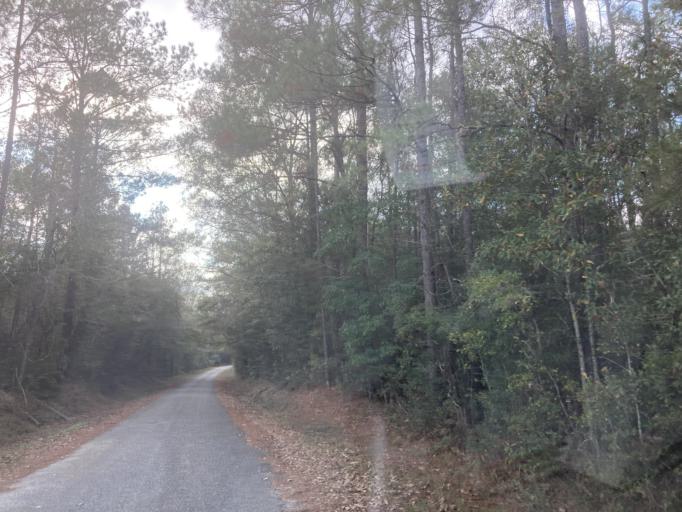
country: US
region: Mississippi
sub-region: Stone County
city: Wiggins
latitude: 30.7997
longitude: -89.1085
